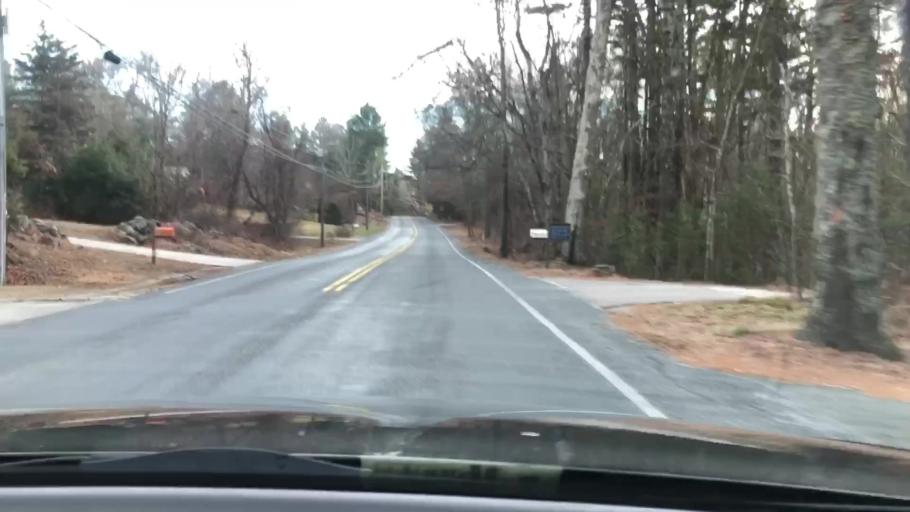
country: US
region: Massachusetts
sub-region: Worcester County
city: Mendon
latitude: 42.0721
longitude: -71.5249
